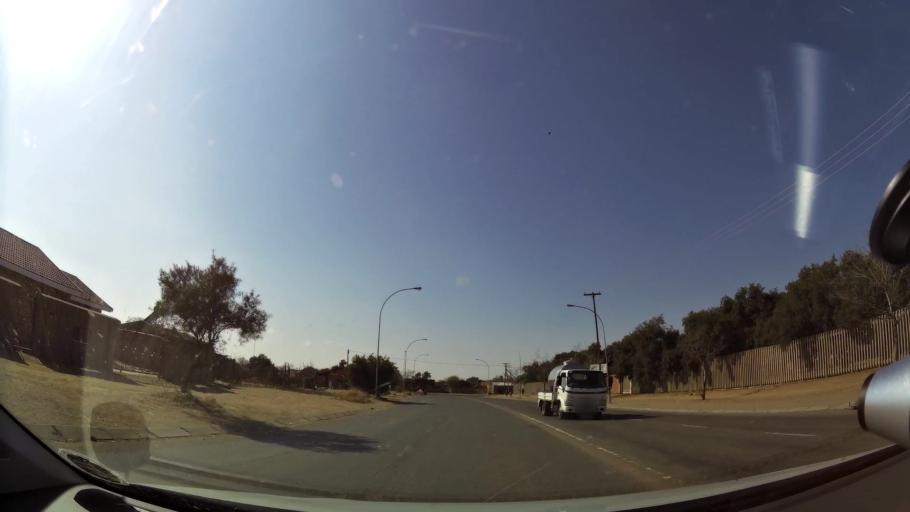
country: ZA
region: Orange Free State
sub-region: Mangaung Metropolitan Municipality
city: Bloemfontein
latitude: -29.1556
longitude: 26.2525
